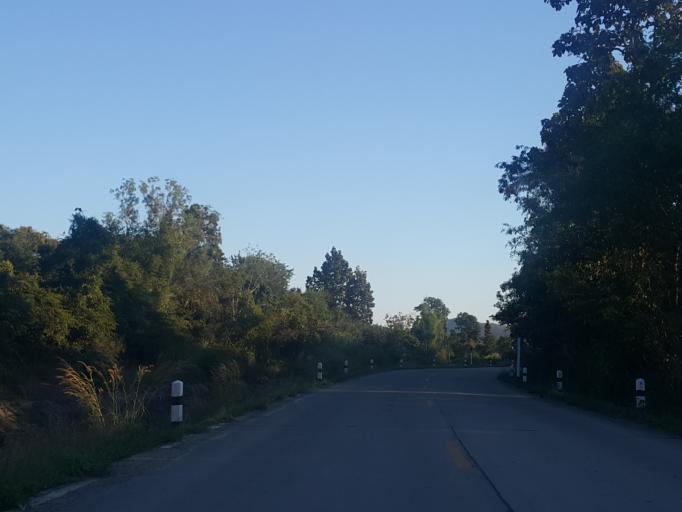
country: TH
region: Chiang Mai
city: San Sai
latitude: 18.8799
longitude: 99.1586
